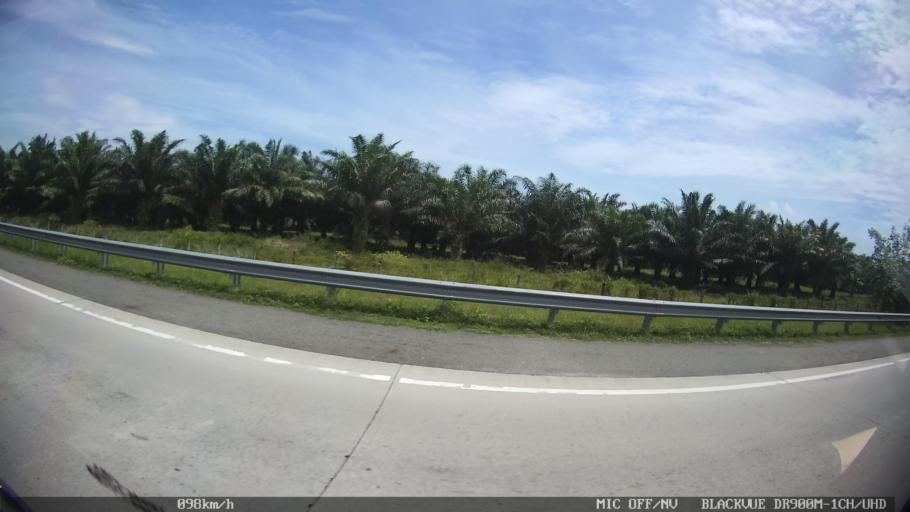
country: ID
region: North Sumatra
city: Perbaungan
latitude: 3.5317
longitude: 98.8780
